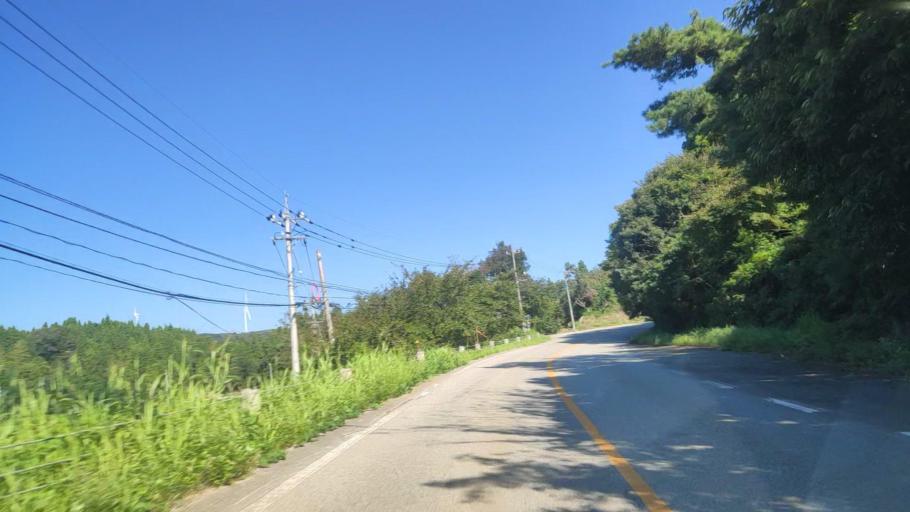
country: JP
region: Ishikawa
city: Nanao
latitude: 37.1654
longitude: 136.7140
